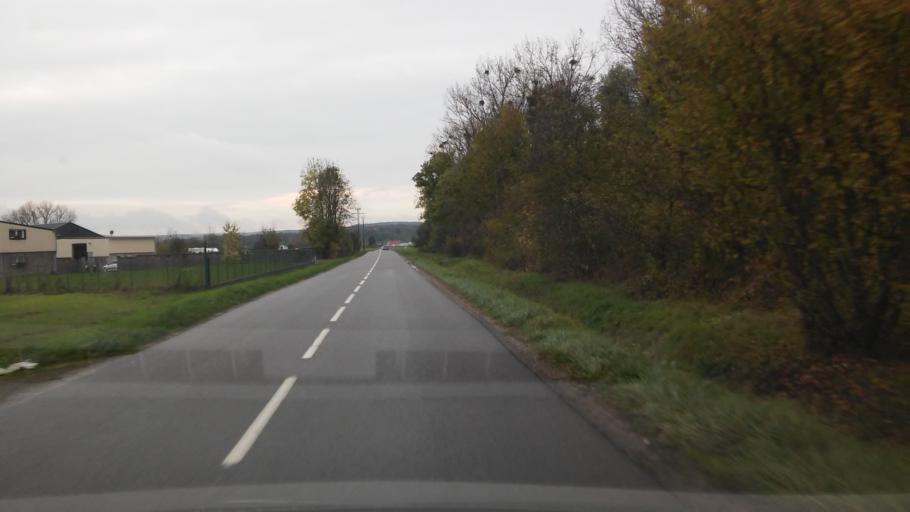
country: FR
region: Lorraine
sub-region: Departement de la Moselle
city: Boulay-Moselle
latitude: 49.1820
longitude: 6.4760
